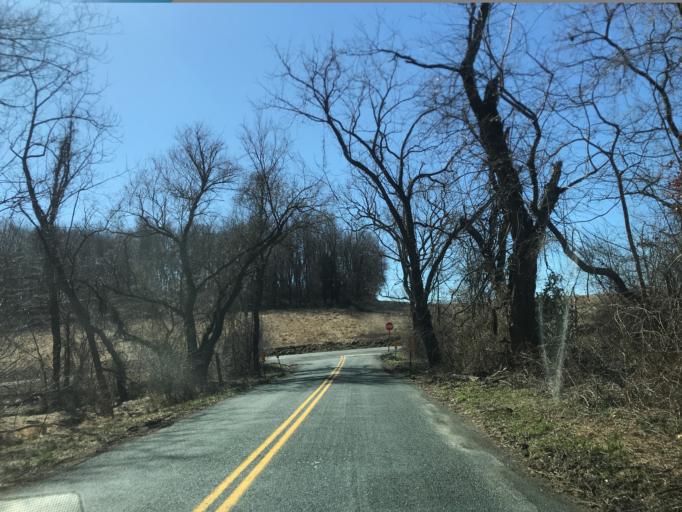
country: US
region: Pennsylvania
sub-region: York County
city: Stewartstown
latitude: 39.7041
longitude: -76.5197
